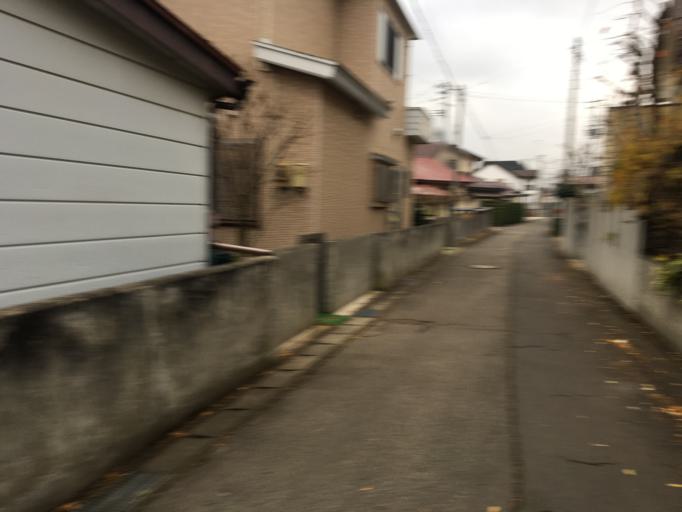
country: JP
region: Aomori
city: Hirosaki
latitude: 40.5936
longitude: 140.4668
